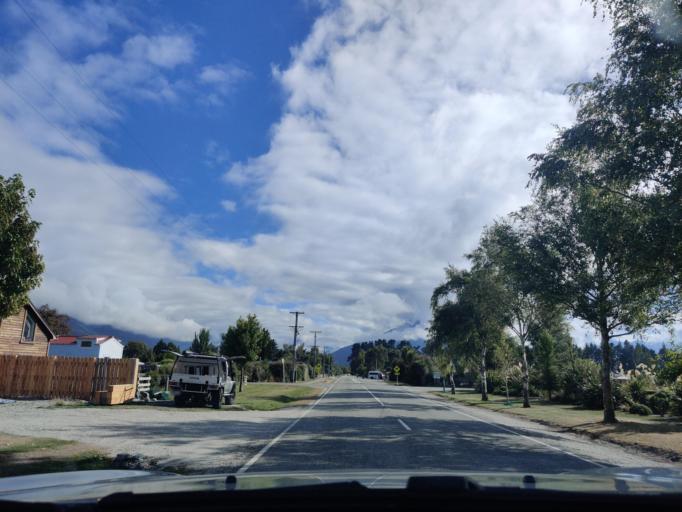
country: NZ
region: Otago
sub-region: Queenstown-Lakes District
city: Queenstown
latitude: -44.8522
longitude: 168.3890
